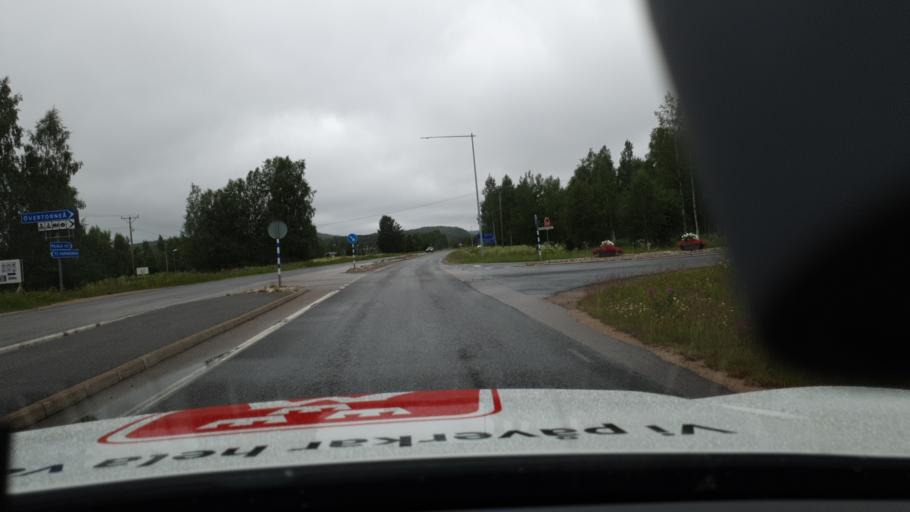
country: SE
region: Norrbotten
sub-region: Overtornea Kommun
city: OEvertornea
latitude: 66.3939
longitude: 23.6307
